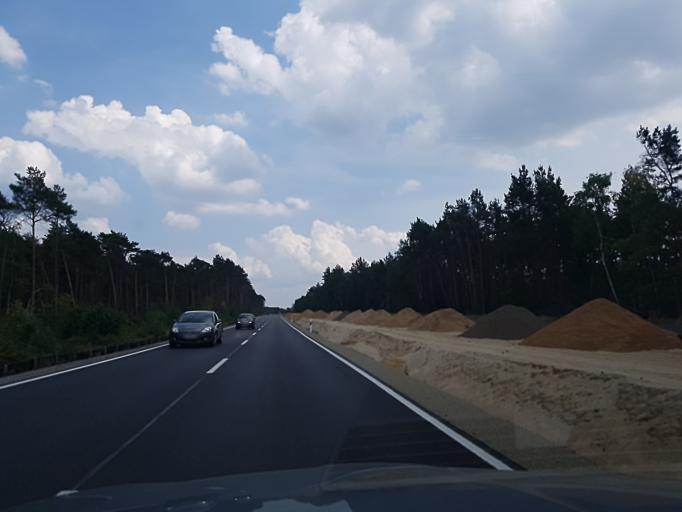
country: DE
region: Brandenburg
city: Bad Liebenwerda
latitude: 51.5088
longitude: 13.4472
